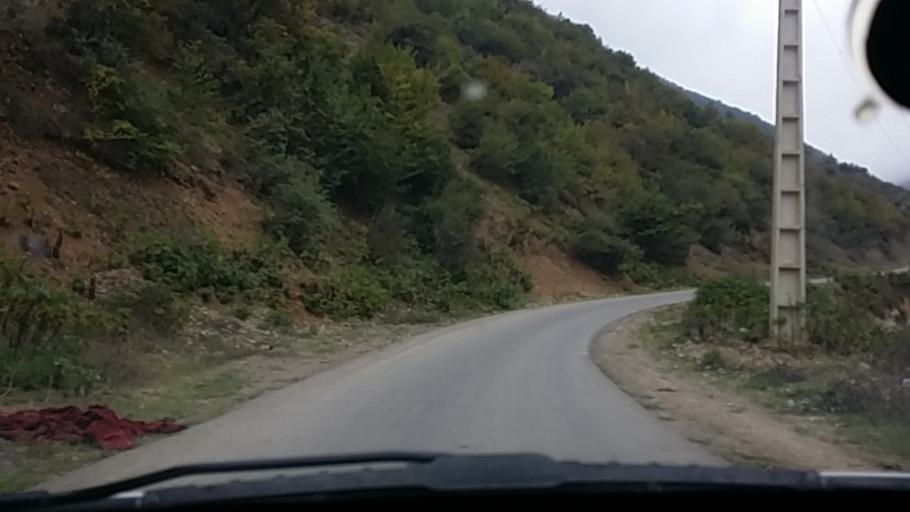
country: IR
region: Mazandaran
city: `Abbasabad
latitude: 36.4667
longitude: 51.1398
